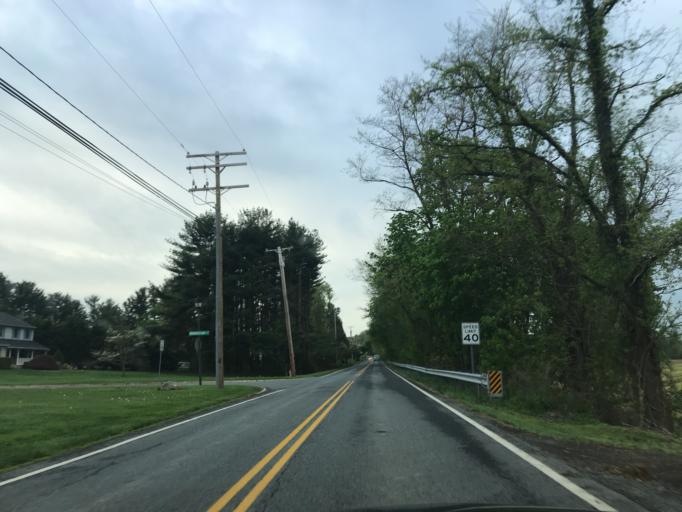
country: US
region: Maryland
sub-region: Harford County
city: Jarrettsville
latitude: 39.6369
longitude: -76.5057
